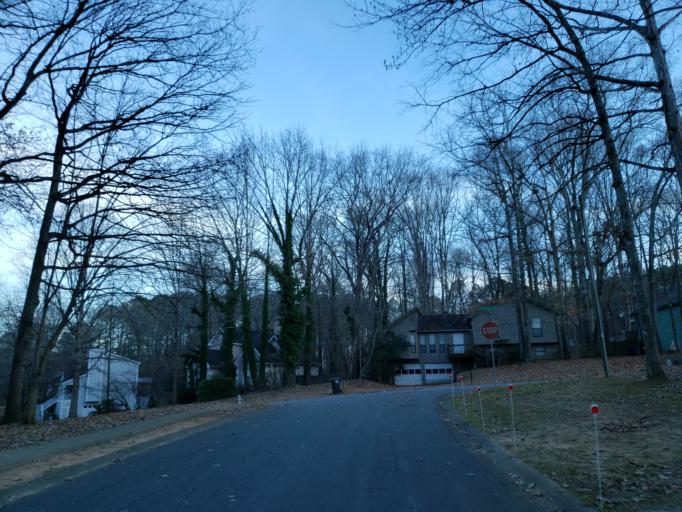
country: US
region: Georgia
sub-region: Cobb County
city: Acworth
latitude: 34.0484
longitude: -84.6481
